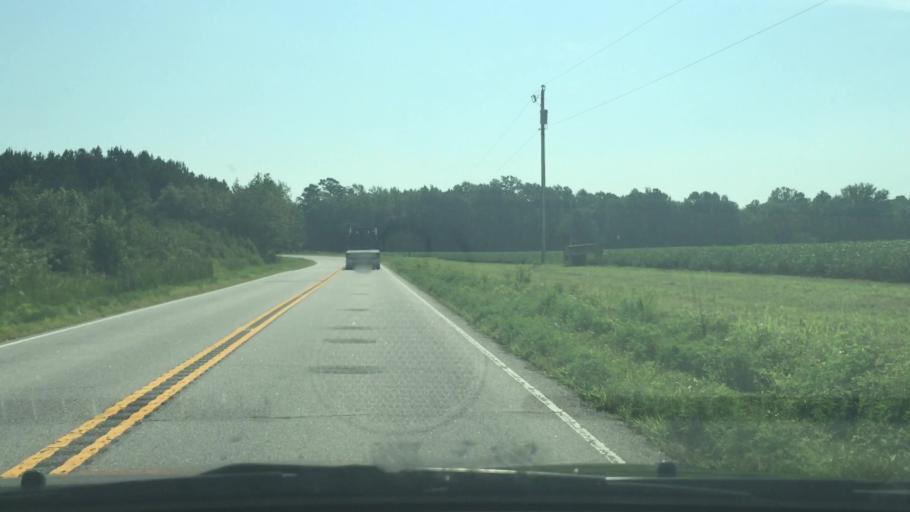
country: US
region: Virginia
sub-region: Sussex County
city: Sussex
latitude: 36.9770
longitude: -77.2226
